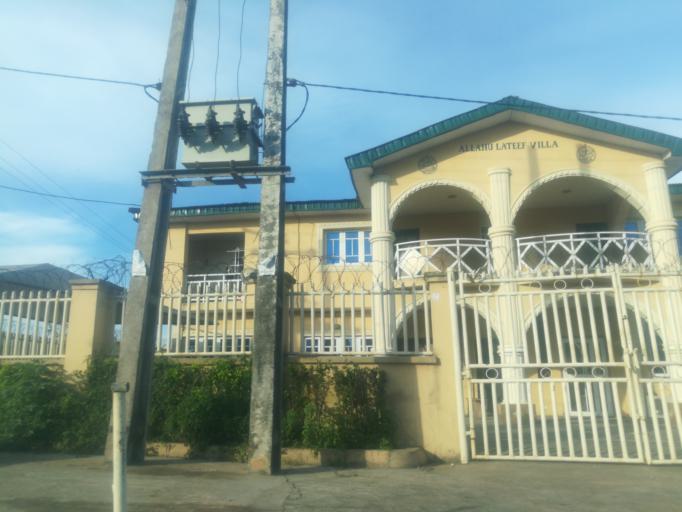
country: NG
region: Oyo
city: Ibadan
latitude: 7.3442
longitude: 3.8863
